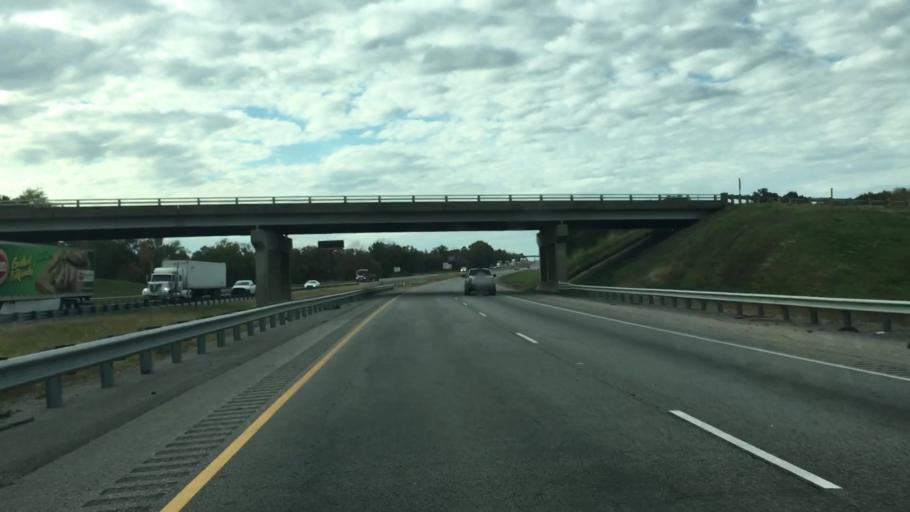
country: US
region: Arkansas
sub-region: Conway County
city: Morrilton
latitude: 35.1750
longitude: -92.7438
